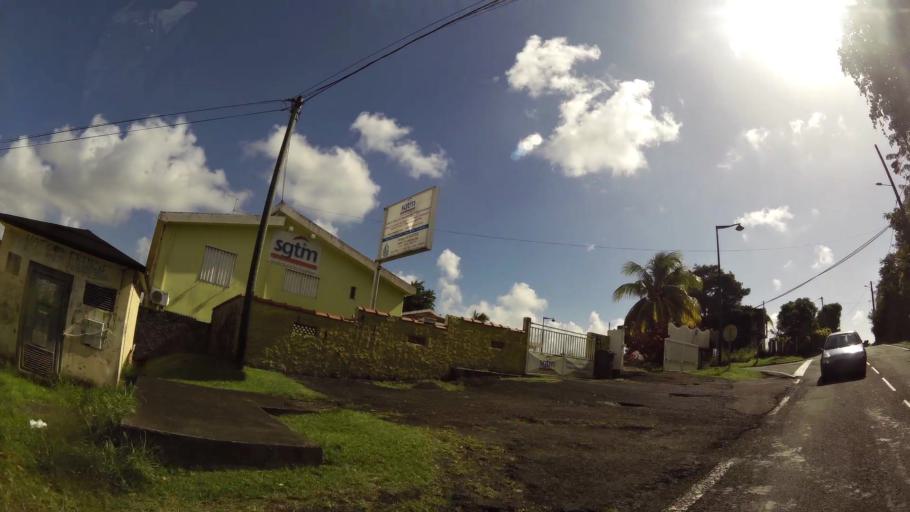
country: MQ
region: Martinique
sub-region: Martinique
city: Fort-de-France
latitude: 14.6237
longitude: -61.0514
